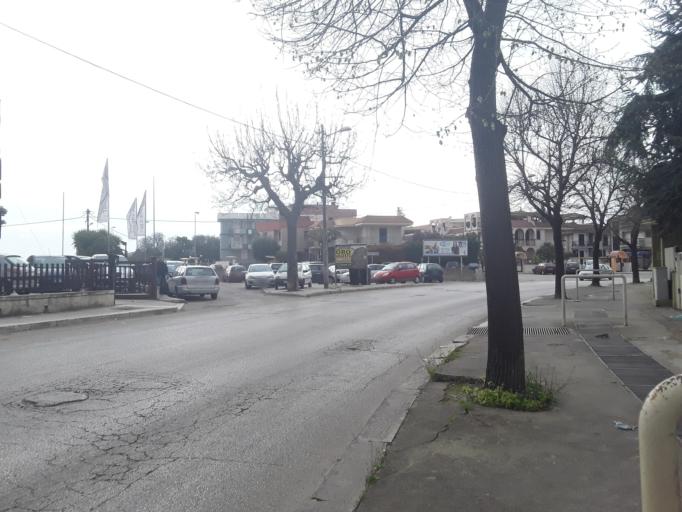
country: IT
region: Apulia
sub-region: Provincia di Bari
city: Ruvo di Puglia
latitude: 41.1169
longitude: 16.4774
